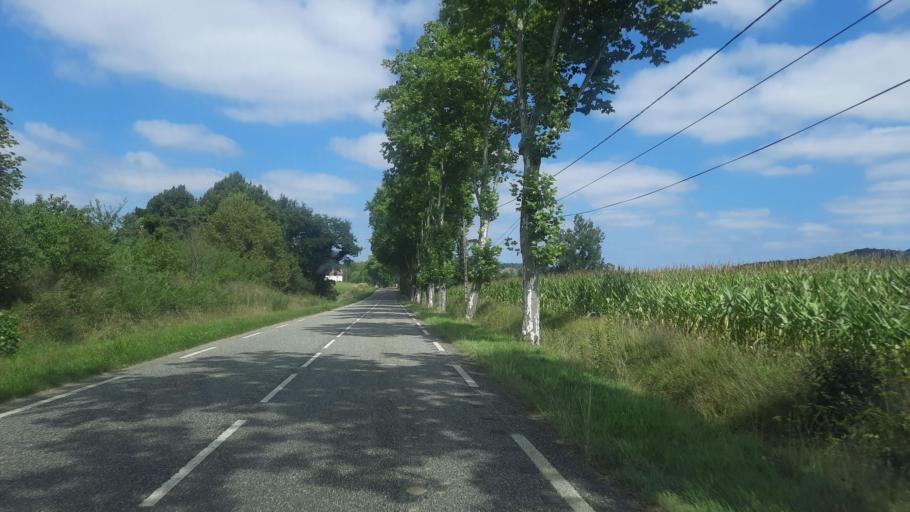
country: FR
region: Midi-Pyrenees
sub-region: Departement de la Haute-Garonne
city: Boulogne-sur-Gesse
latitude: 43.3622
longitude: 0.7363
